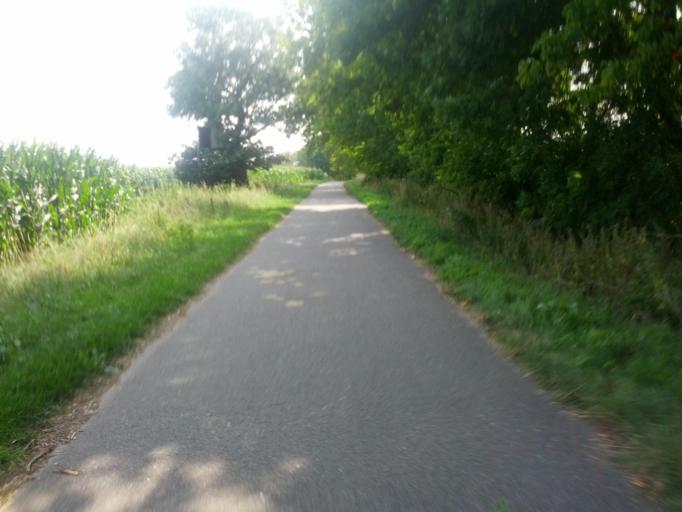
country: DE
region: Mecklenburg-Vorpommern
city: Bastorf
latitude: 54.1238
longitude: 11.6808
